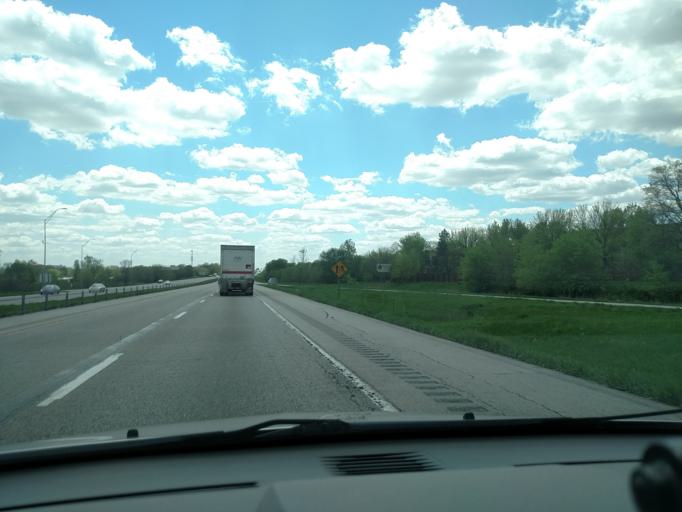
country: US
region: Iowa
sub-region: Polk County
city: Ankeny
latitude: 41.7298
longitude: -93.5771
